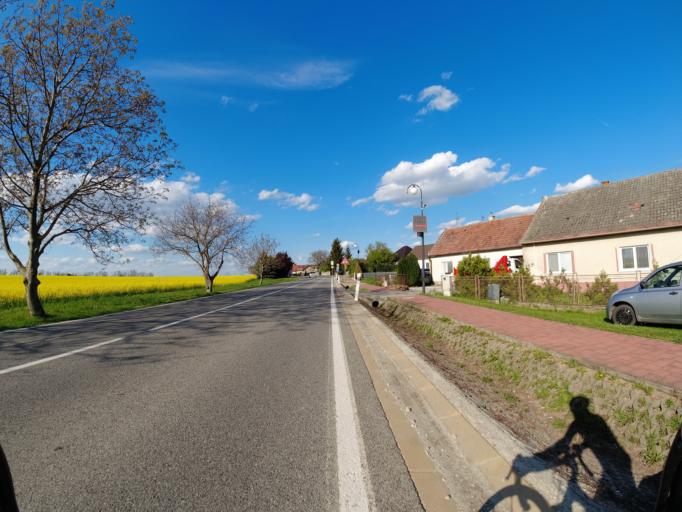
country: SK
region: Trnavsky
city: Leopoldov
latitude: 48.4829
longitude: 17.7142
